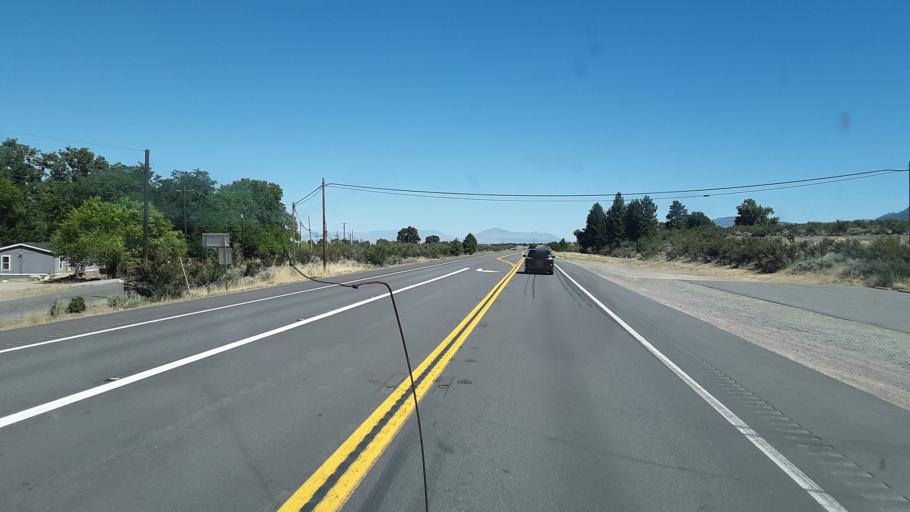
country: US
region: California
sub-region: Lassen County
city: Janesville
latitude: 40.2902
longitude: -120.5009
